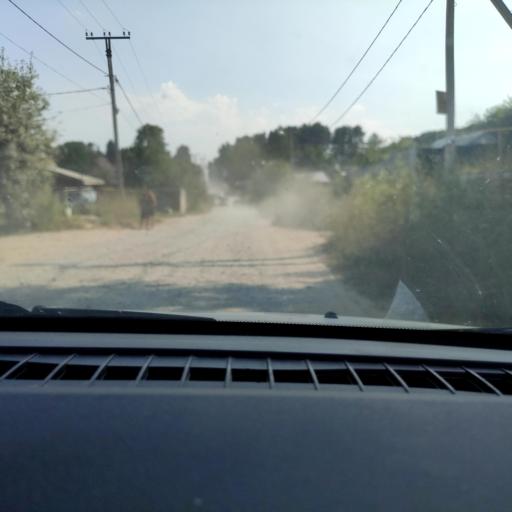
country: RU
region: Perm
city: Polazna
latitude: 58.1383
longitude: 56.4573
